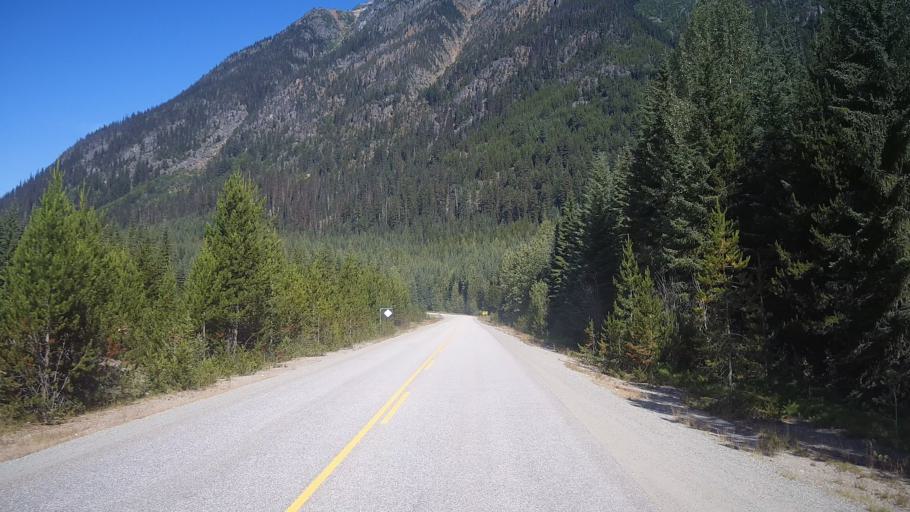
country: CA
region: British Columbia
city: Pemberton
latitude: 50.3856
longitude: -122.3668
